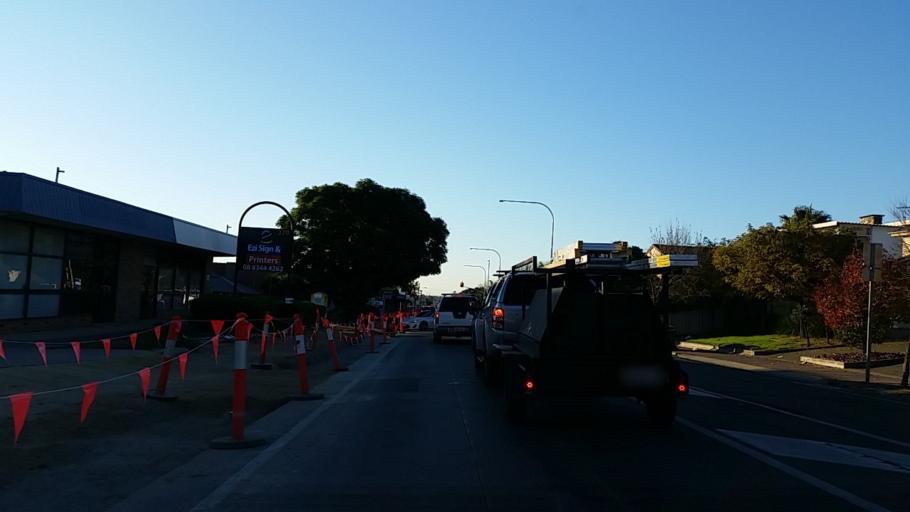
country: AU
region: South Australia
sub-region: Prospect
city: Prospect
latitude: -34.8755
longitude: 138.5932
